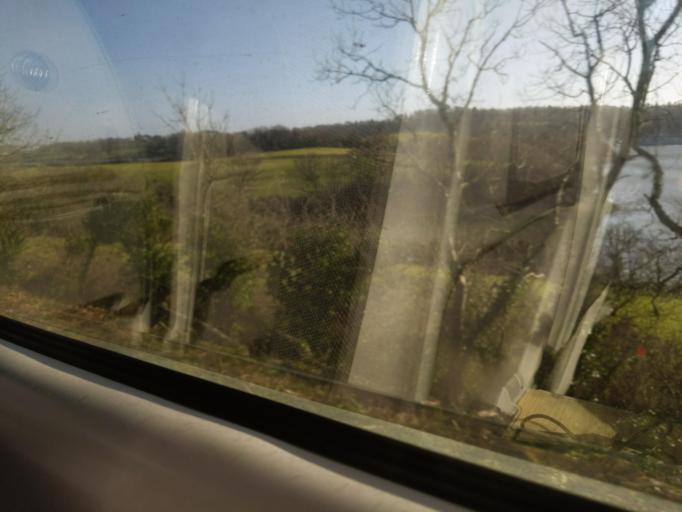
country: GB
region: England
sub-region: Cornwall
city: Saltash
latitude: 50.3977
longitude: -4.2312
